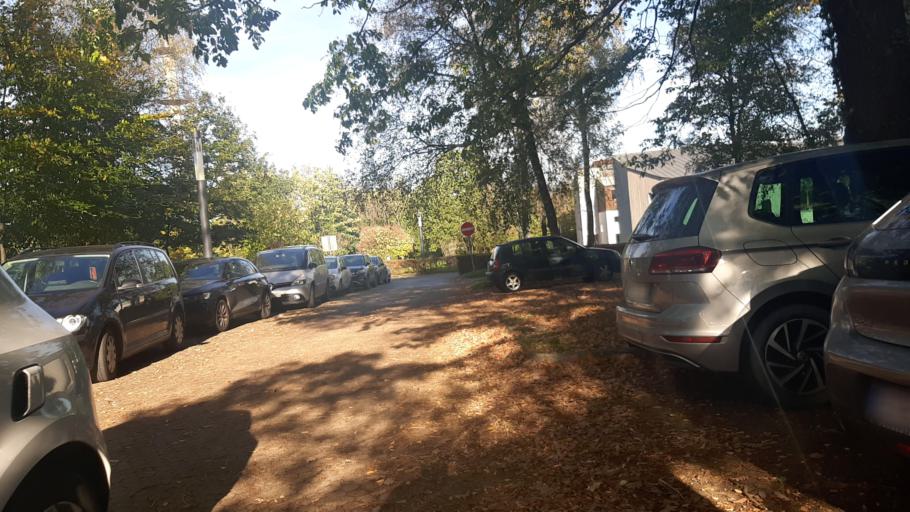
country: BE
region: Wallonia
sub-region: Province de Liege
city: Liege
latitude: 50.5857
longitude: 5.5595
